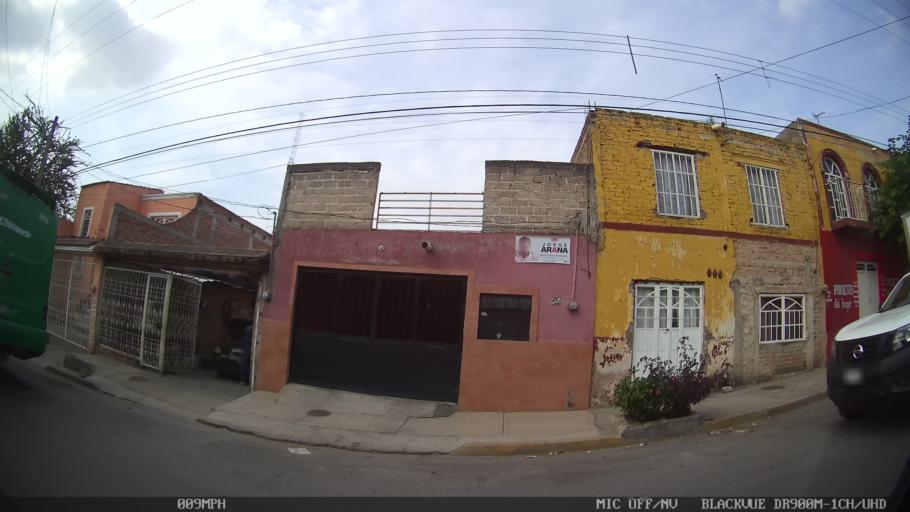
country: MX
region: Jalisco
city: Tonala
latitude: 20.6206
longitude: -103.2348
